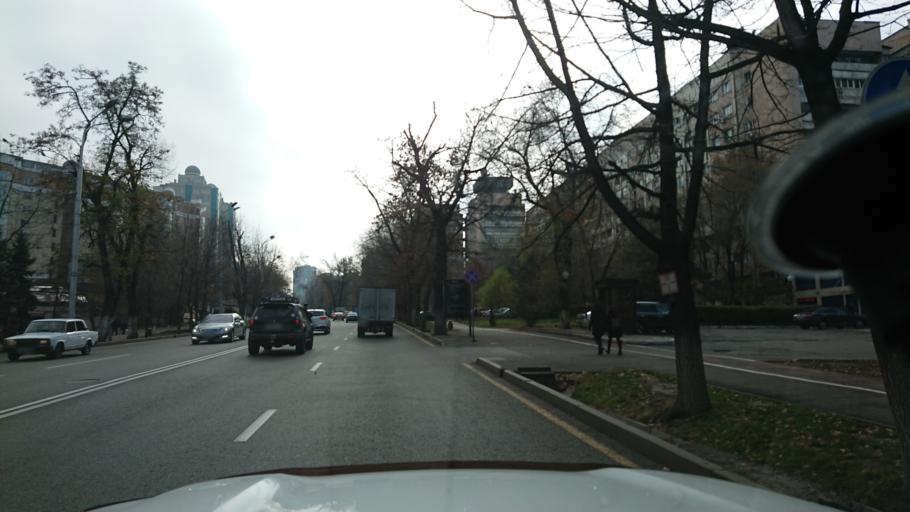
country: KZ
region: Almaty Qalasy
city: Almaty
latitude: 43.2372
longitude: 76.9575
